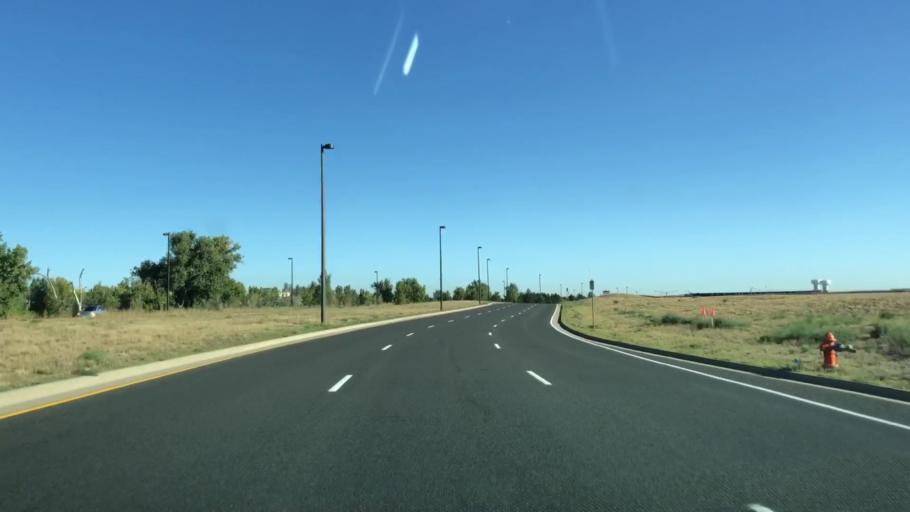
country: US
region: Colorado
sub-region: Larimer County
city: Loveland
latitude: 40.4127
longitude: -104.9866
